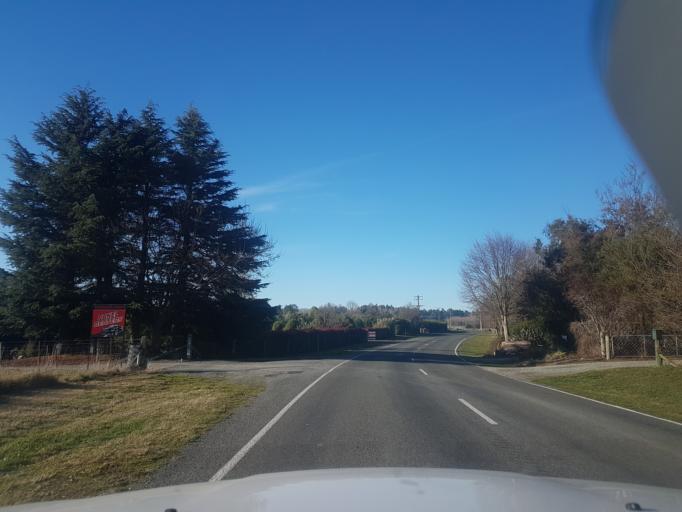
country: NZ
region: Canterbury
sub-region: Timaru District
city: Pleasant Point
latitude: -44.2566
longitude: 171.1275
